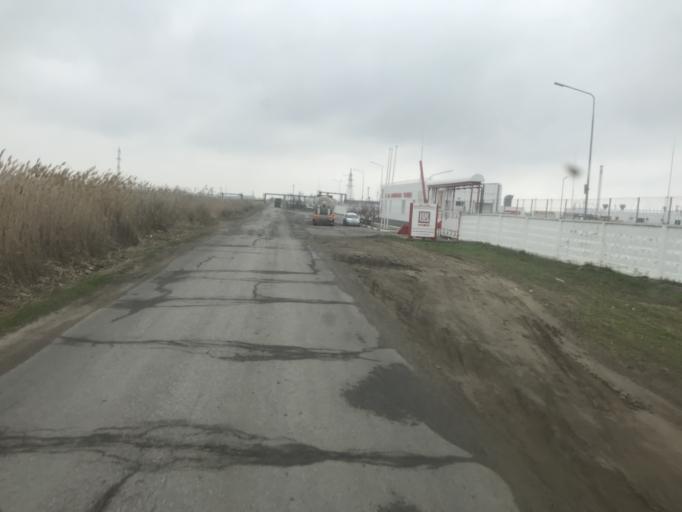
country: RU
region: Volgograd
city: Svetlyy Yar
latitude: 48.5117
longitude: 44.6371
